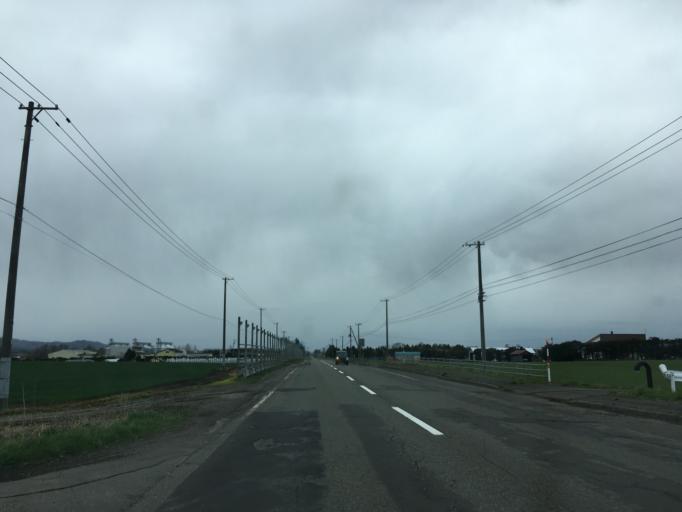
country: JP
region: Hokkaido
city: Chitose
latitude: 42.9282
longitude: 141.8074
